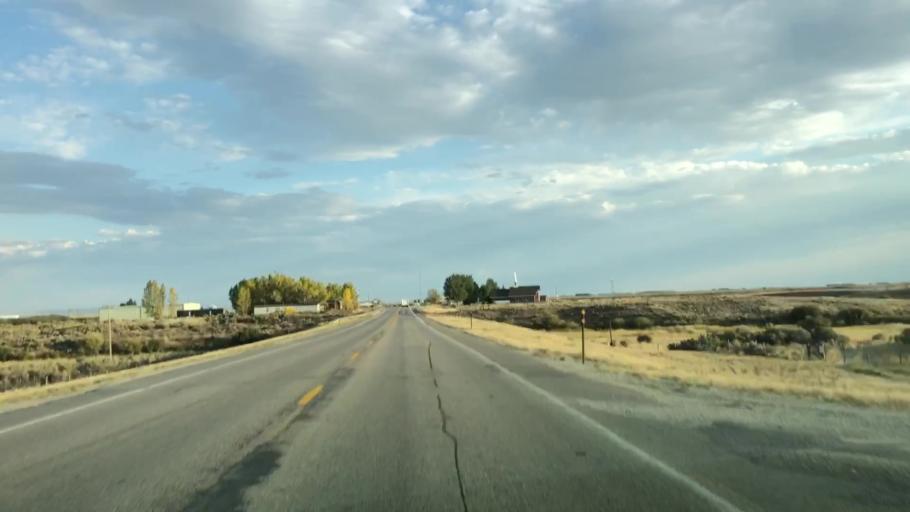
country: US
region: Wyoming
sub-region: Sweetwater County
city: North Rock Springs
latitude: 42.1153
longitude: -109.4512
